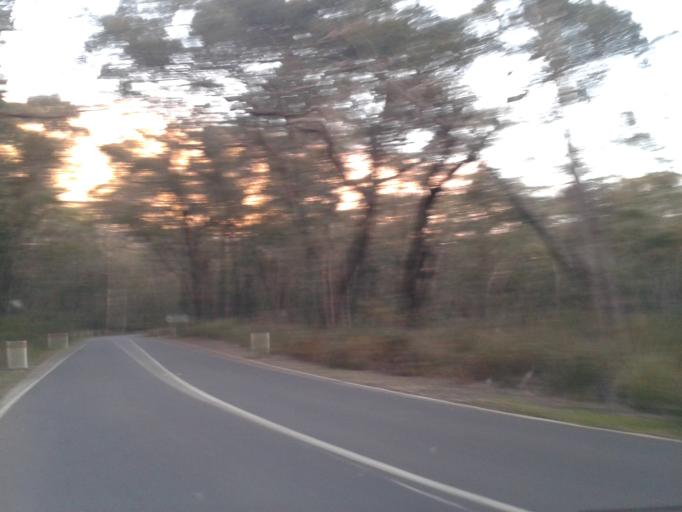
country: AU
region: Victoria
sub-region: Northern Grampians
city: Stawell
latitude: -37.1459
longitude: 142.4674
